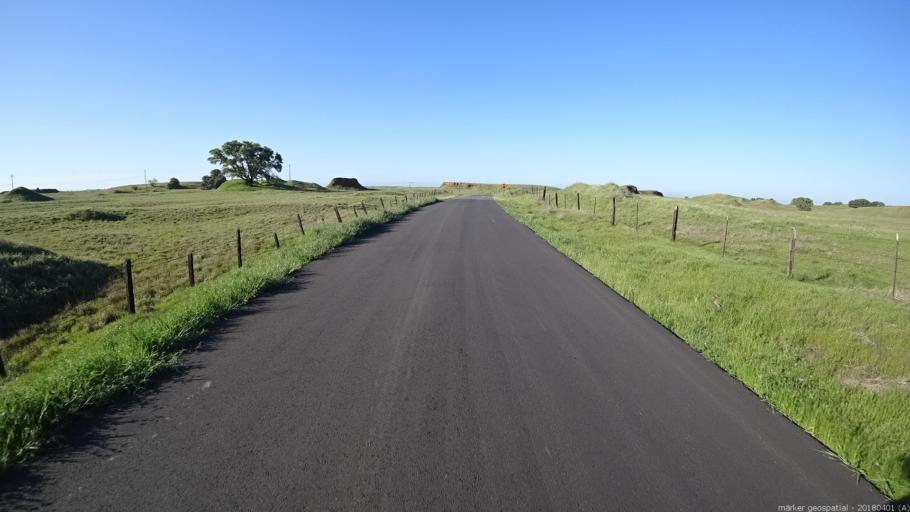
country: US
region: California
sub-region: Sacramento County
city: Rancho Murieta
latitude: 38.4878
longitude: -121.0517
